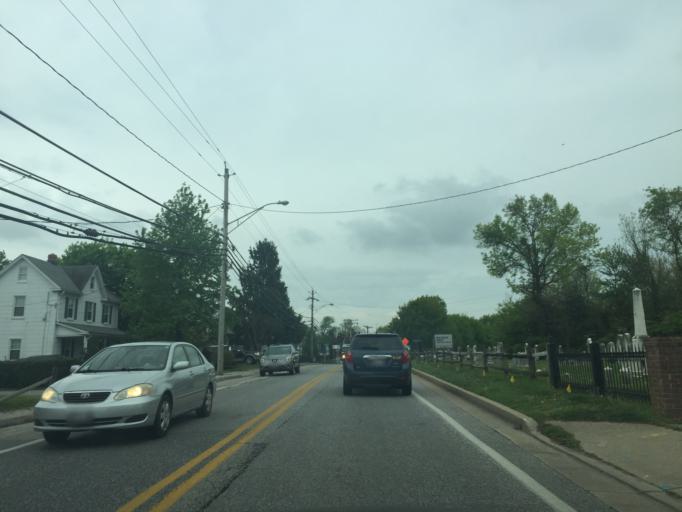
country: US
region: Maryland
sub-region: Baltimore County
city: Catonsville
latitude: 39.2848
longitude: -76.7309
